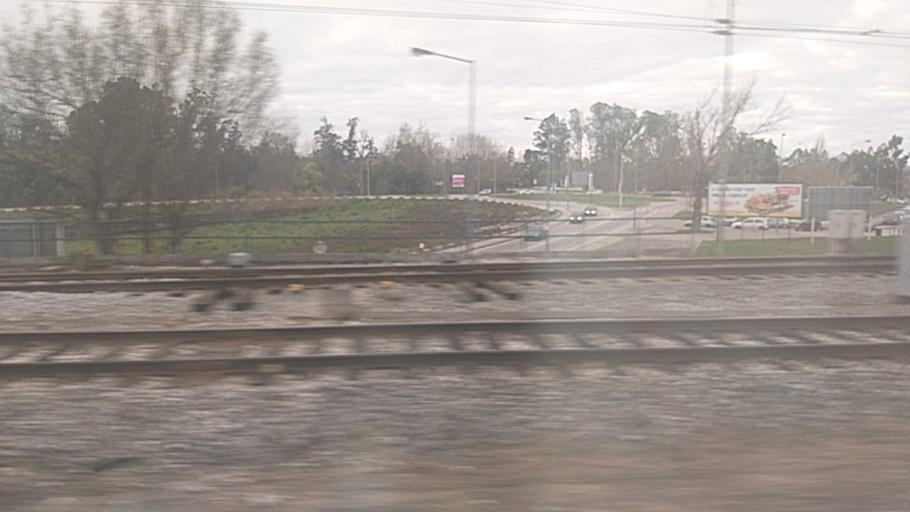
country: PT
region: Coimbra
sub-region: Coimbra
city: Coimbra
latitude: 40.2240
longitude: -8.4404
